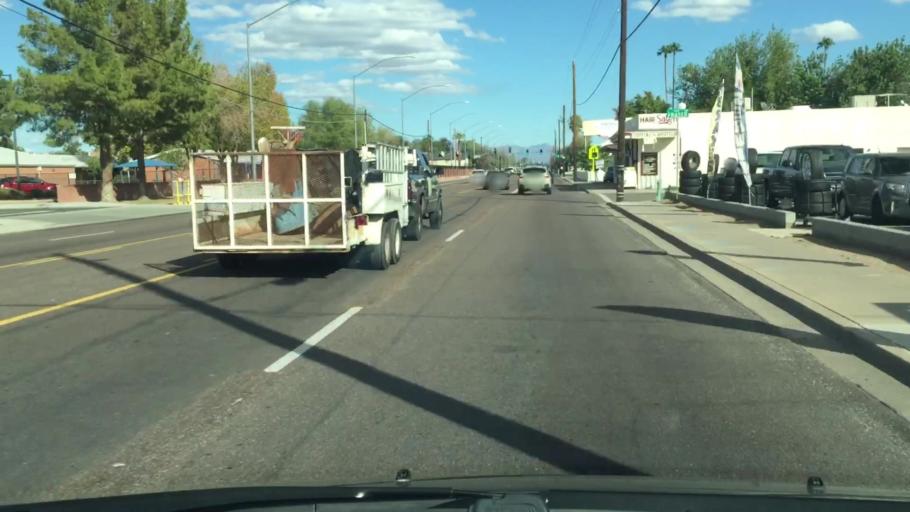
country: US
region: Arizona
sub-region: Maricopa County
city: Mesa
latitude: 33.4083
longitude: -111.8124
